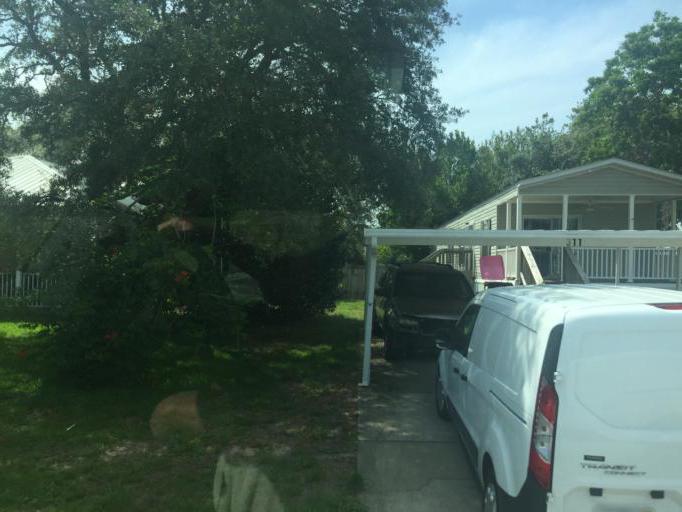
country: US
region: Florida
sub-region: Bay County
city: Laguna Beach
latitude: 30.2488
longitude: -85.9324
